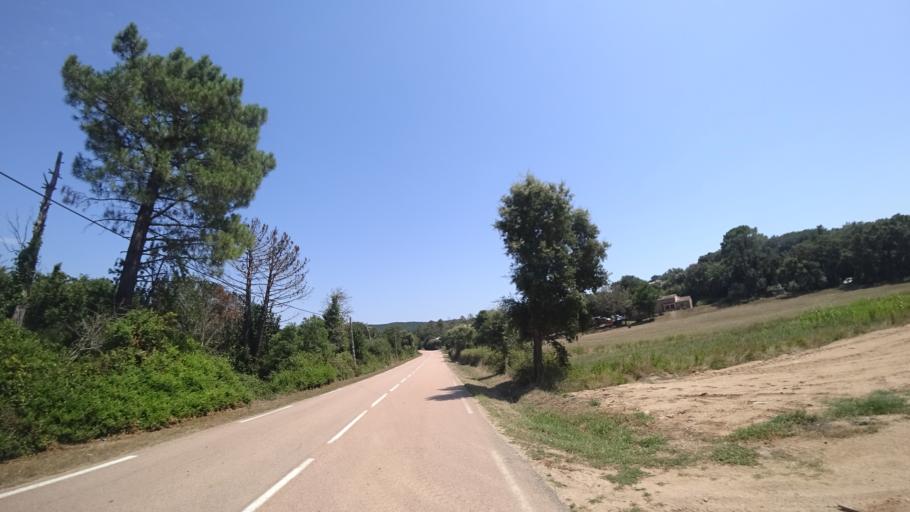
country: FR
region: Corsica
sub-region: Departement de la Corse-du-Sud
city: Porto-Vecchio
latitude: 41.6280
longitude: 9.2476
